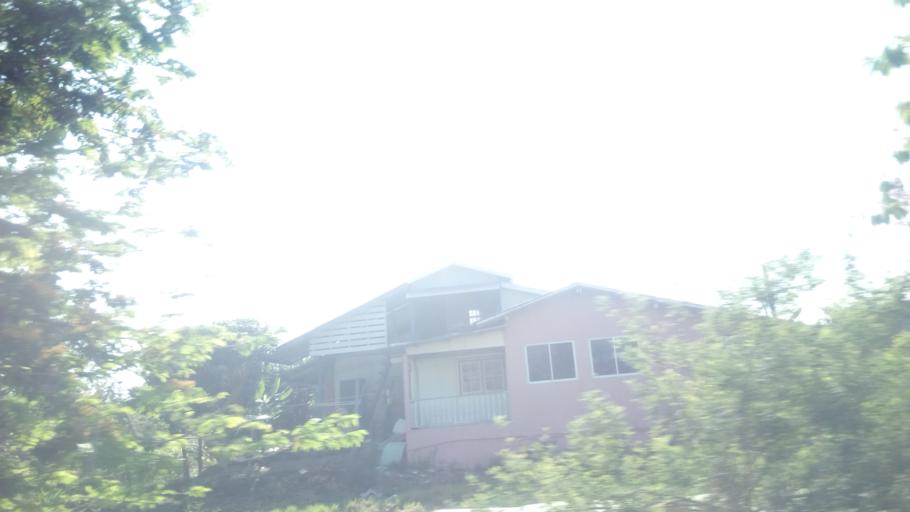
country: TH
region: Nakhon Pathom
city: Salaya
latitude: 13.8182
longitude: 100.3090
